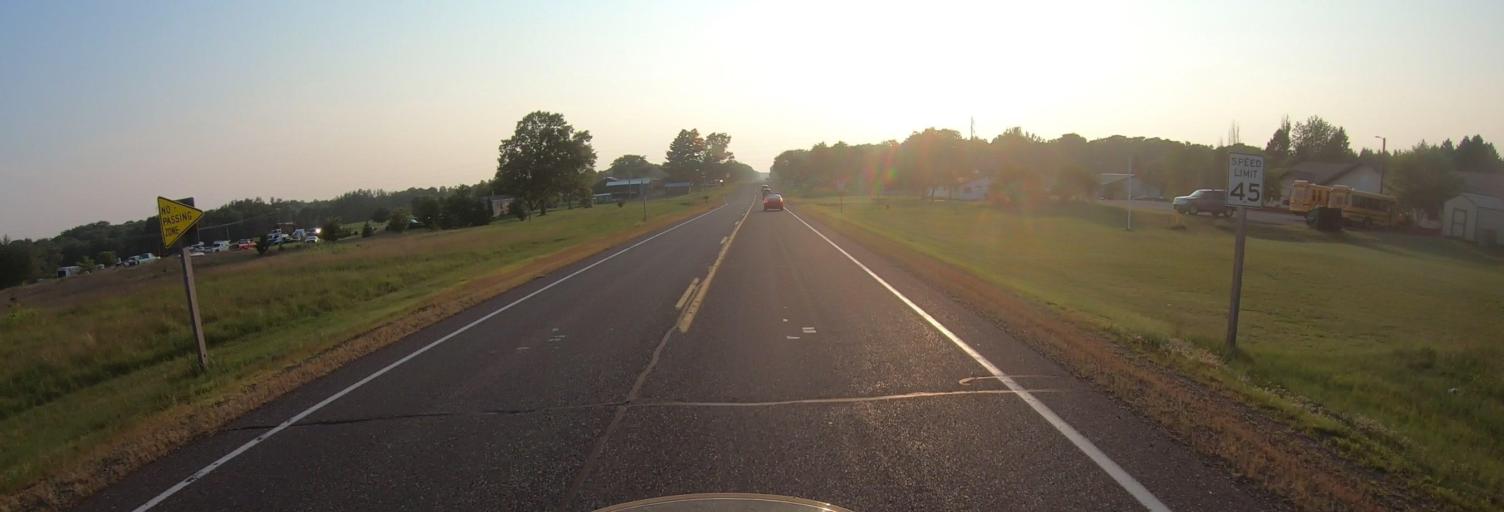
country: US
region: Wisconsin
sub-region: Burnett County
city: Siren
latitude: 45.8088
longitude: -92.1722
